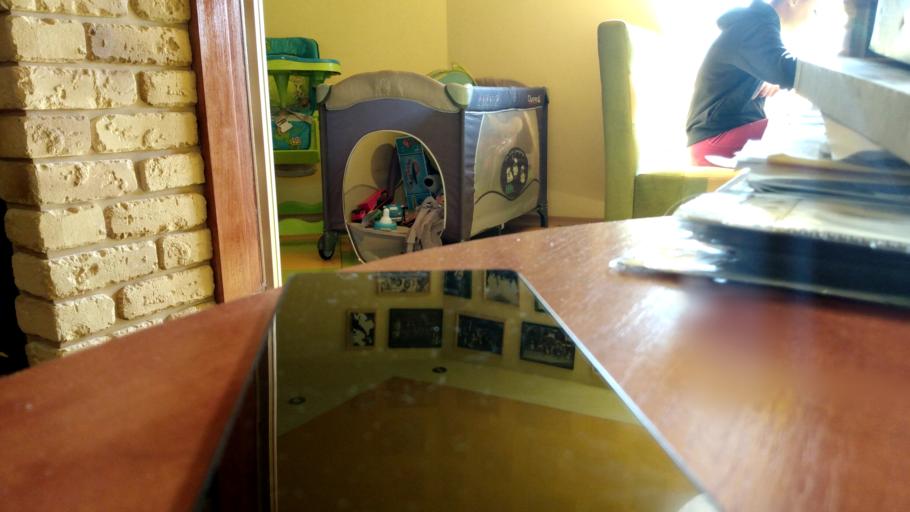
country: RU
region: Penza
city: Serdobsk
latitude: 52.4672
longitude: 44.2802
